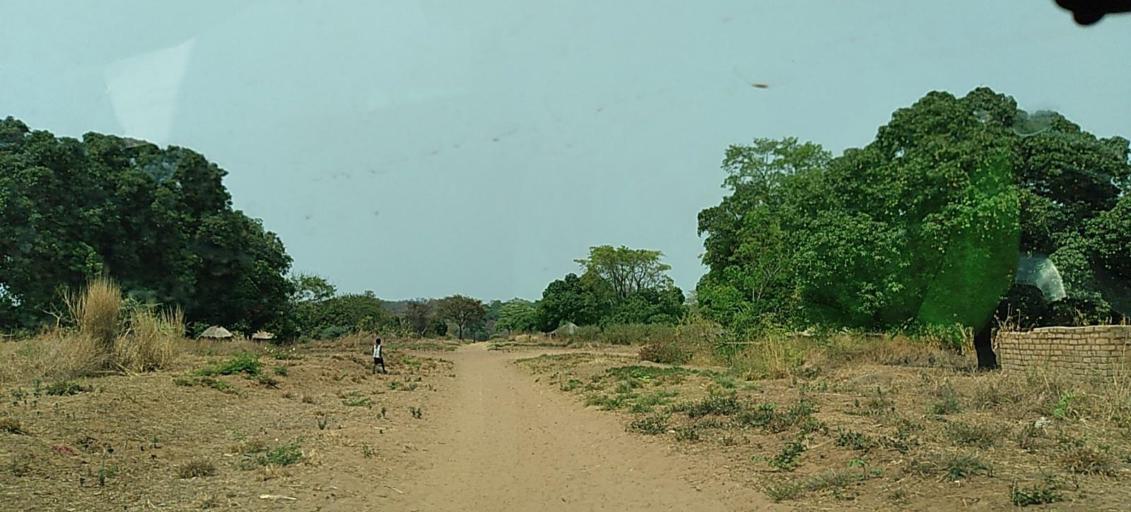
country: ZM
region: Western
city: Lukulu
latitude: -13.9788
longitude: 23.2287
